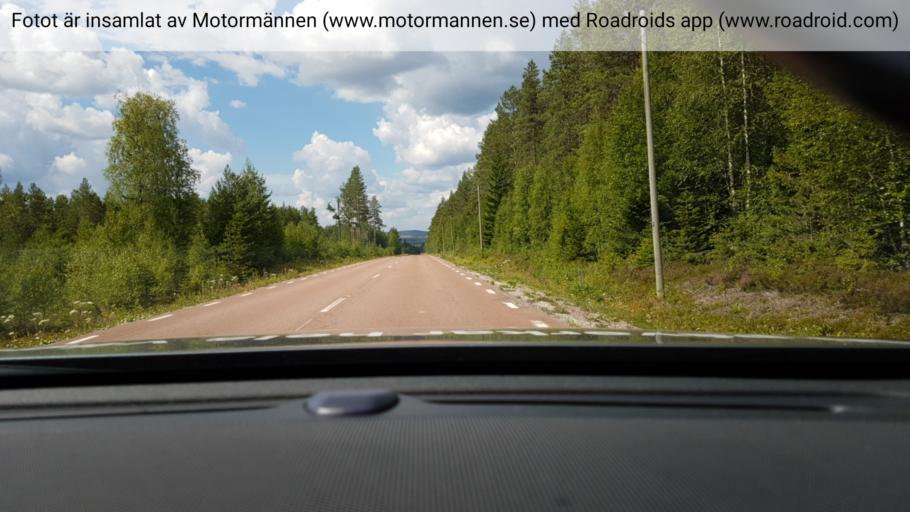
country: SE
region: Dalarna
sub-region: Faluns Kommun
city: Bjursas
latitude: 61.0301
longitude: 15.5379
